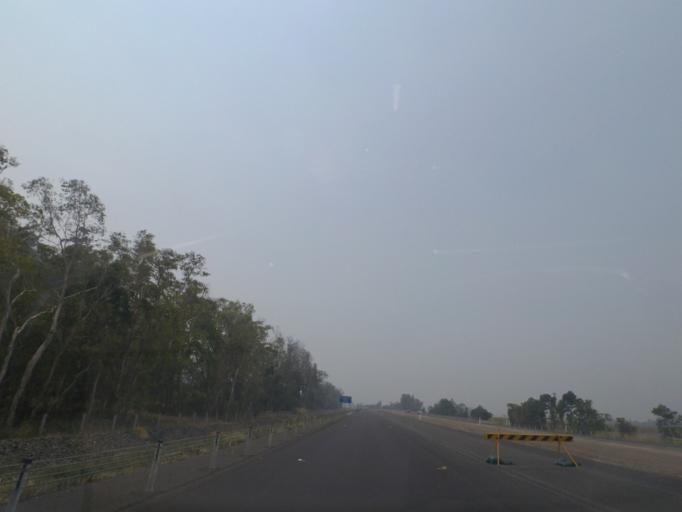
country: AU
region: New South Wales
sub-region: Ballina
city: Ballina
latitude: -28.8807
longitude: 153.4860
